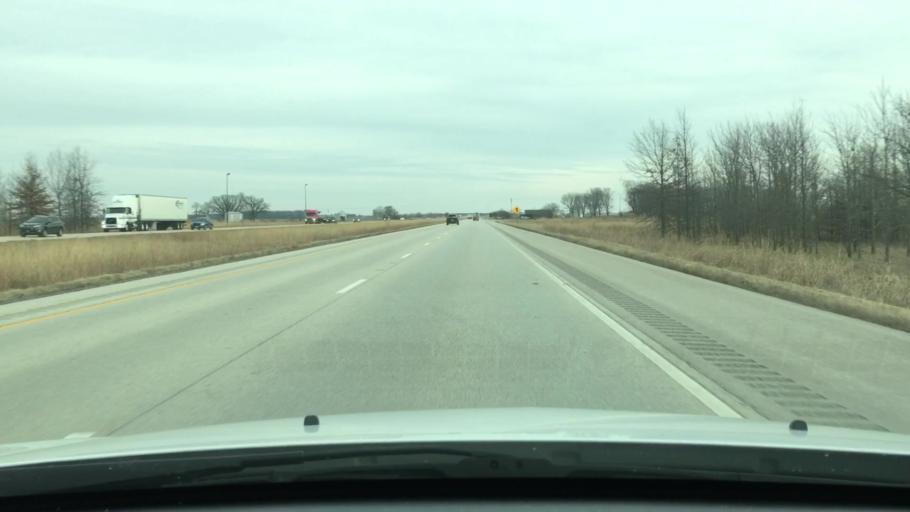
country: US
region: Illinois
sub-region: Sangamon County
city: New Berlin
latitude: 39.7400
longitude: -89.9223
